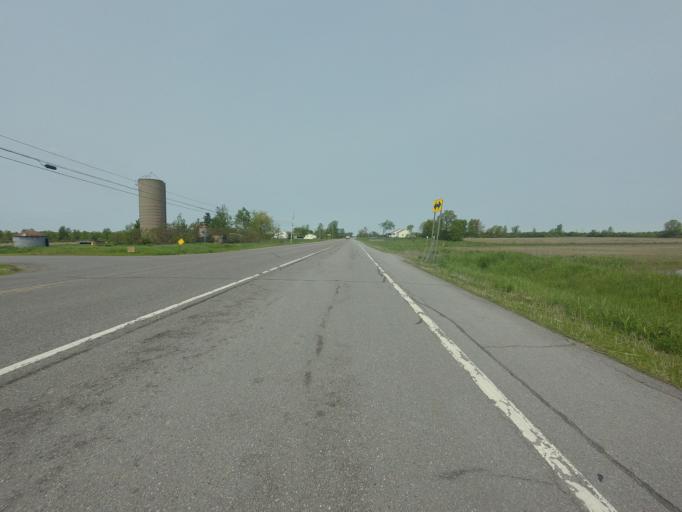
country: US
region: New York
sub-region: Jefferson County
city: Dexter
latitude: 44.0313
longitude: -76.0529
